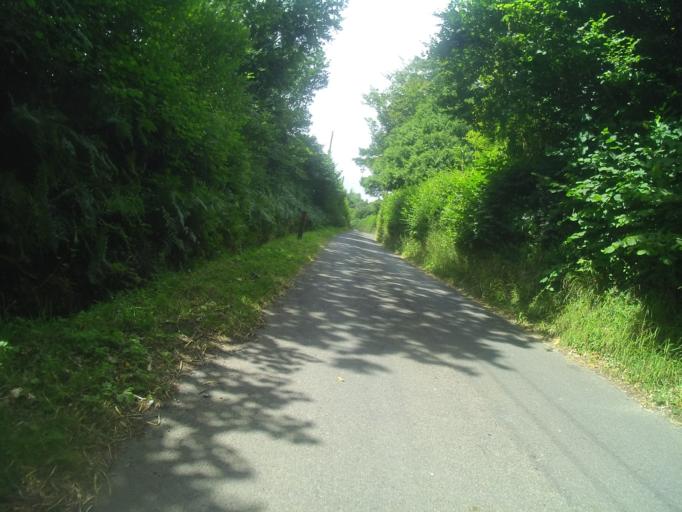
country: GB
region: England
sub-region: Devon
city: Buckfastleigh
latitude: 50.5125
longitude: -3.8275
